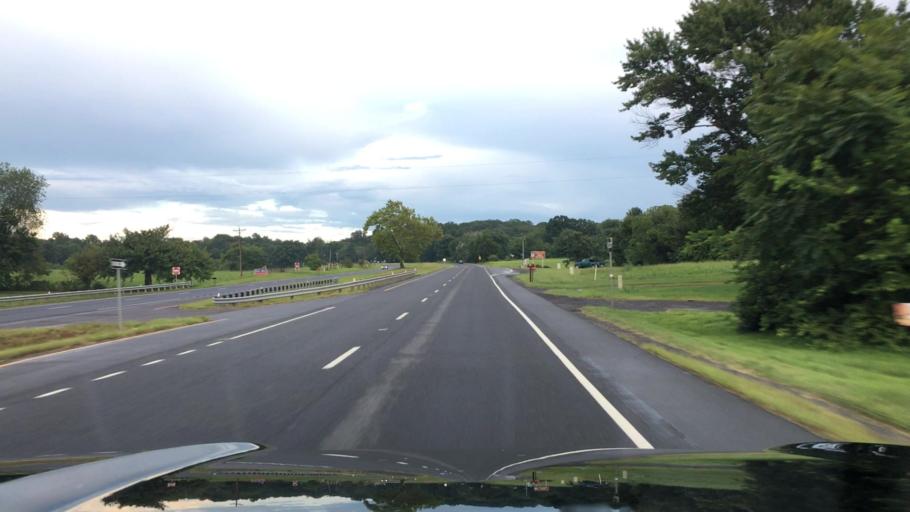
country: US
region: Virginia
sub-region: Culpeper County
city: Merrimac
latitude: 38.4524
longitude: -78.1036
